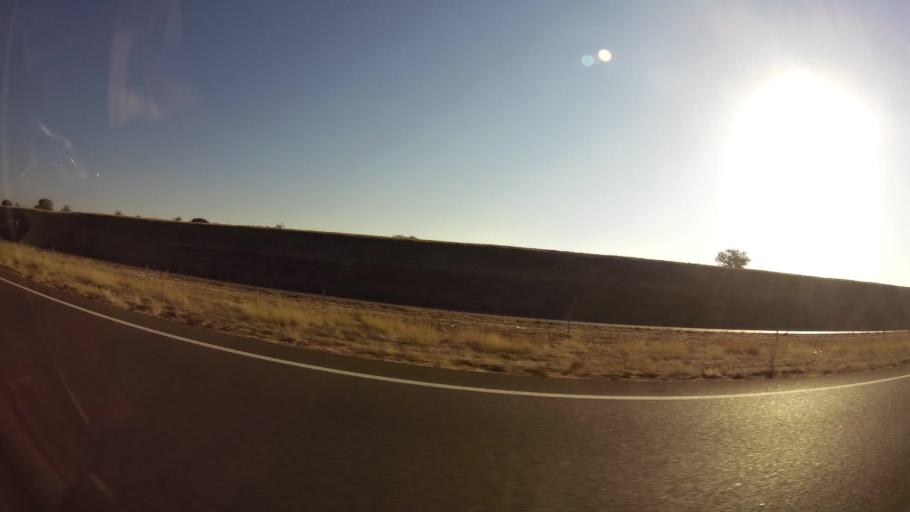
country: ZA
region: Gauteng
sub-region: City of Tshwane Metropolitan Municipality
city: Pretoria
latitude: -25.6400
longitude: 28.2164
